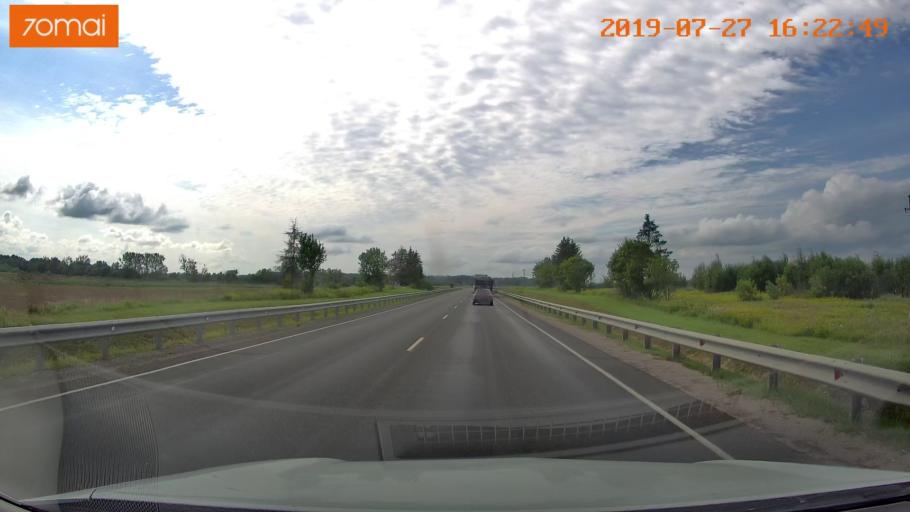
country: RU
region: Kaliningrad
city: Zheleznodorozhnyy
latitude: 54.6294
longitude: 21.4862
